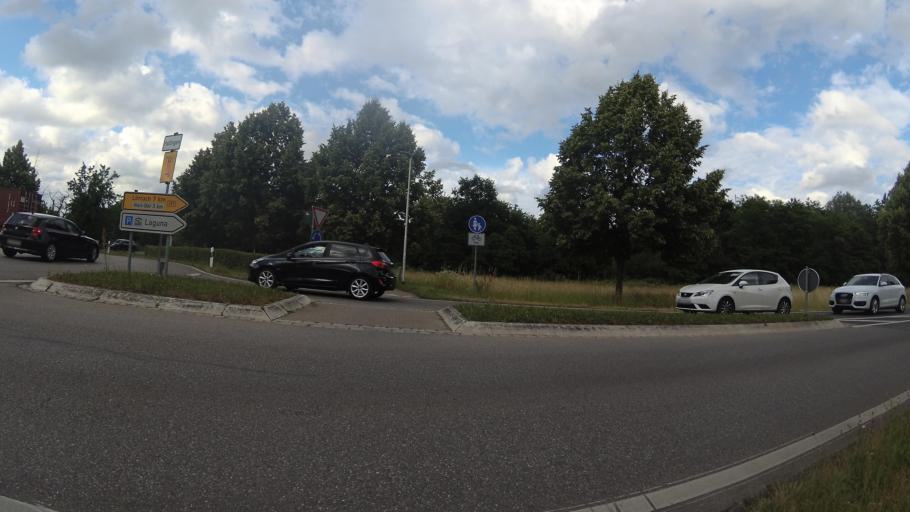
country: DE
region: Baden-Wuerttemberg
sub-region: Freiburg Region
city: Weil am Rhein
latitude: 47.5893
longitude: 7.6079
